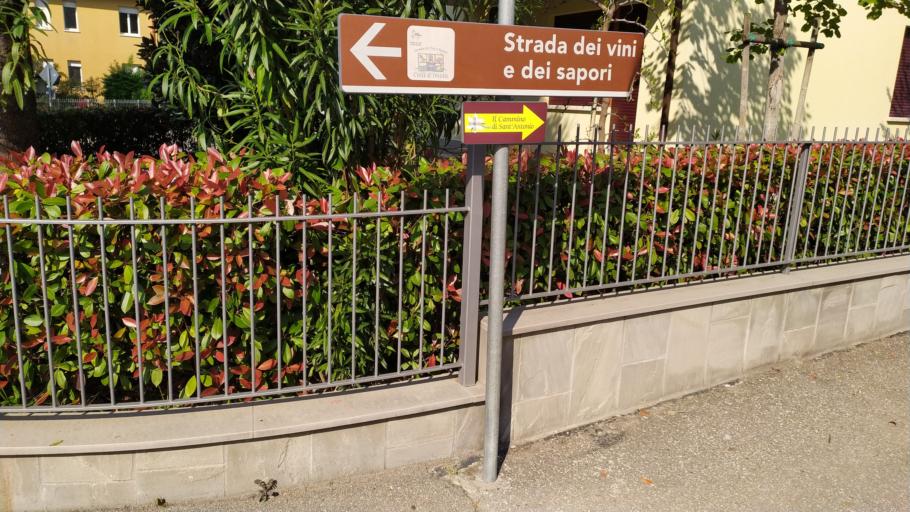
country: IT
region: Emilia-Romagna
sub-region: Provincia di Bologna
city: Borgo Tossignano
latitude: 44.2764
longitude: 11.5927
